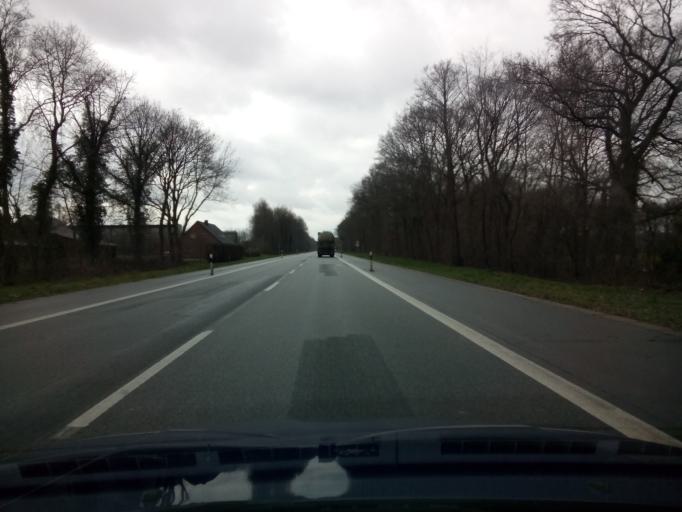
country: DE
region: Lower Saxony
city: Wildeshausen
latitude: 52.9392
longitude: 8.4743
